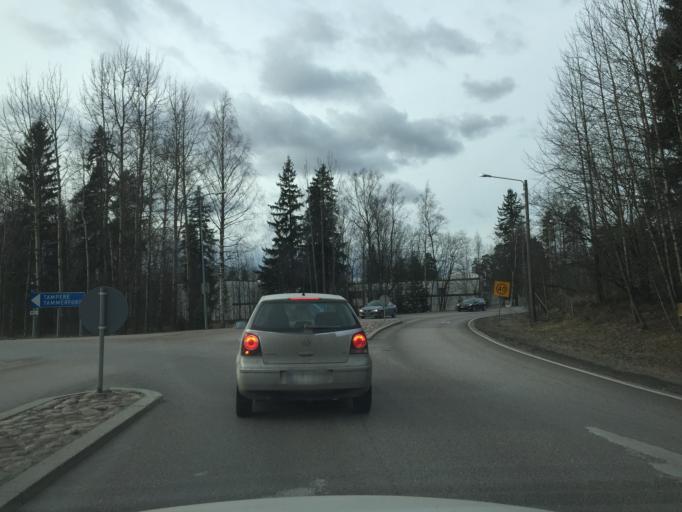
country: FI
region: Uusimaa
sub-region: Helsinki
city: Helsinki
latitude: 60.2369
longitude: 24.9020
